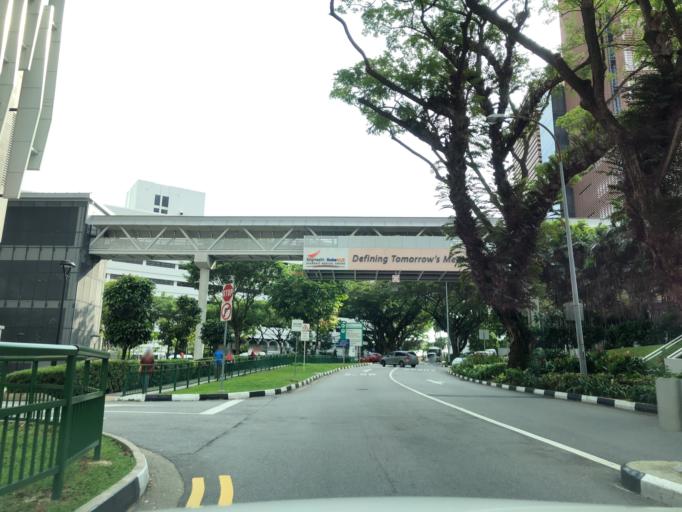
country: SG
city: Singapore
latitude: 1.2818
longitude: 103.8351
